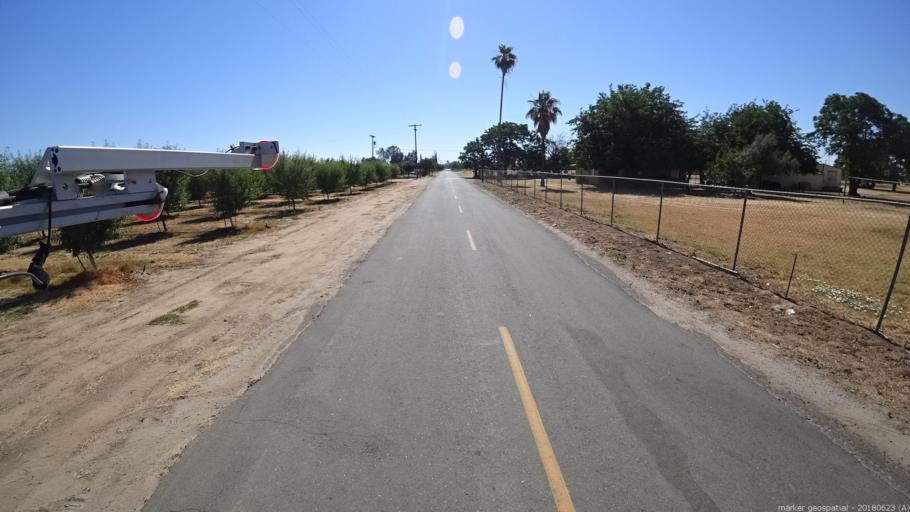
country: US
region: California
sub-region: Madera County
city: Parksdale
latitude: 36.9816
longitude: -120.0159
